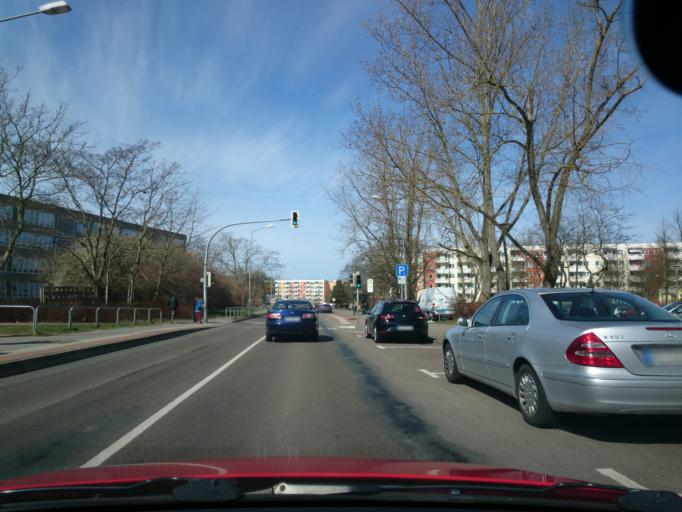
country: DE
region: Mecklenburg-Vorpommern
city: Lambrechtshagen
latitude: 54.1160
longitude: 12.0546
